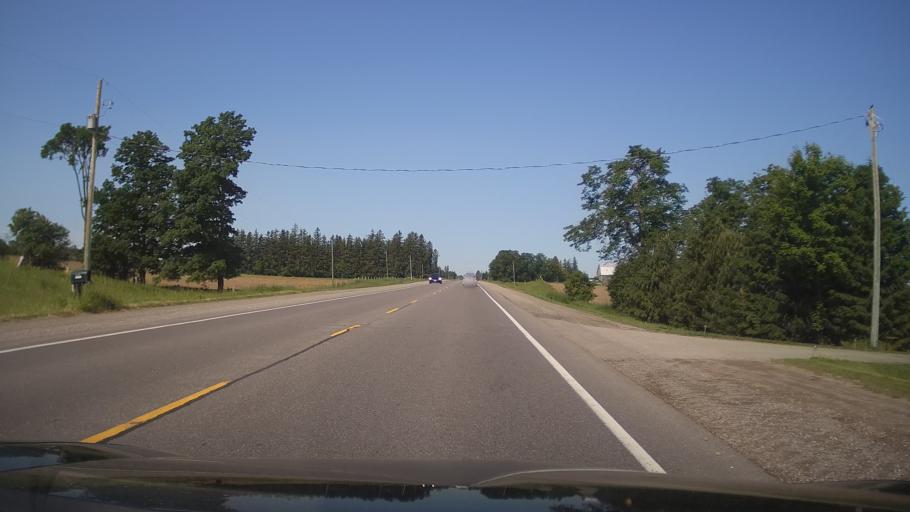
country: CA
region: Ontario
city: Omemee
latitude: 44.3446
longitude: -78.8281
